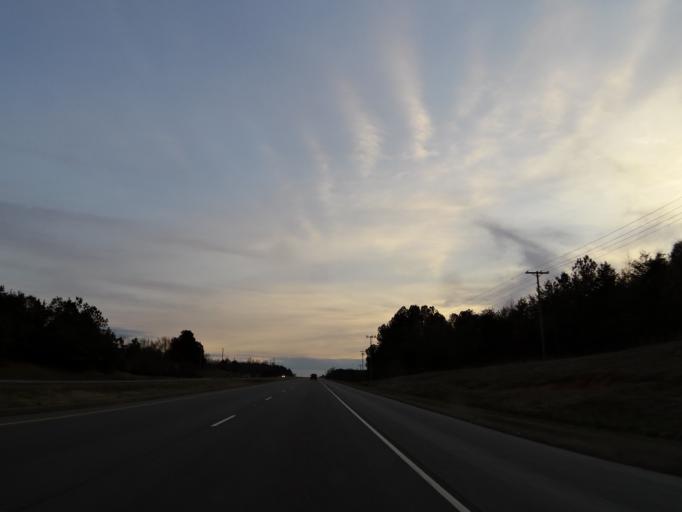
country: US
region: Tennessee
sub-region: McMinn County
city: Englewood
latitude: 35.3926
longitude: -84.5025
